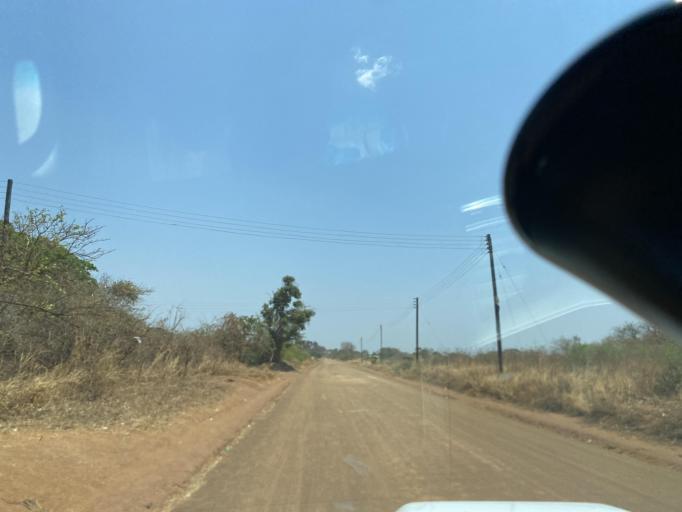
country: ZM
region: Lusaka
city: Lusaka
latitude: -15.4216
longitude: 28.0987
